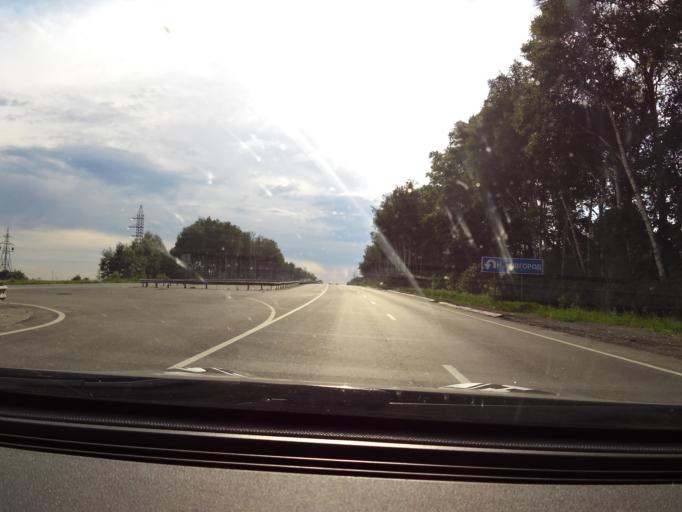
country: RU
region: Vladimir
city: Gorokhovets
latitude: 56.1597
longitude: 42.5456
